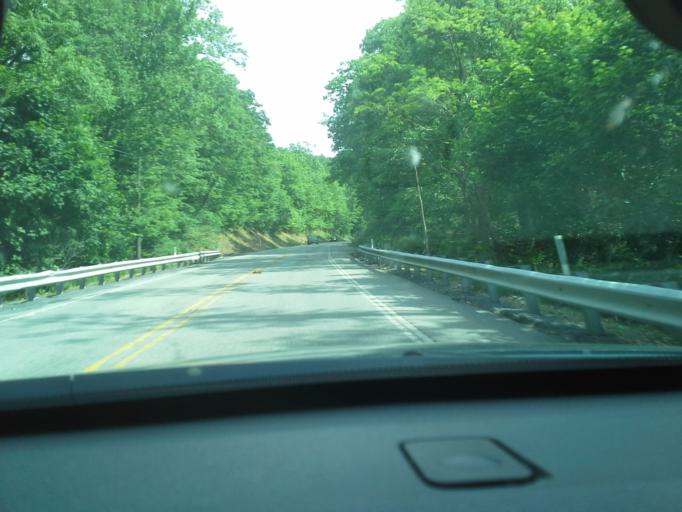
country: US
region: Pennsylvania
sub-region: Fulton County
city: McConnellsburg
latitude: 39.9134
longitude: -77.9671
